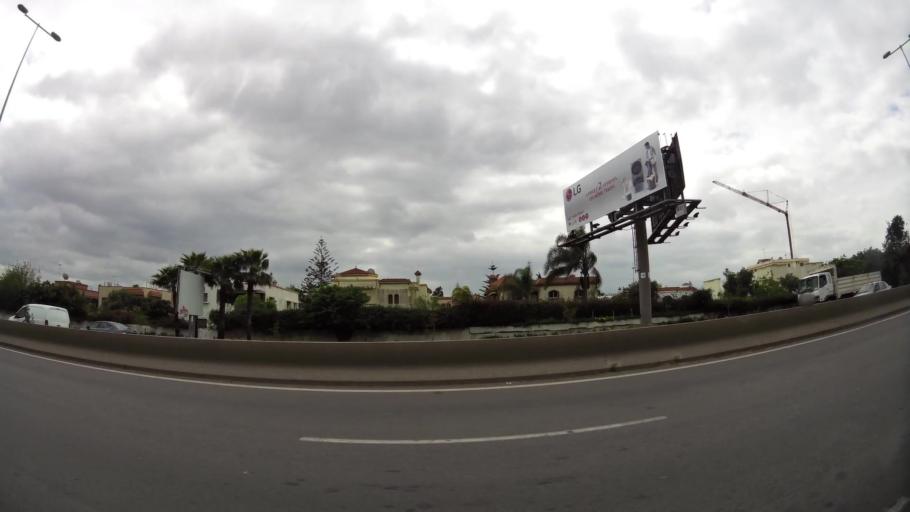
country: MA
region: Grand Casablanca
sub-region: Casablanca
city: Casablanca
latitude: 33.5526
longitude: -7.6285
